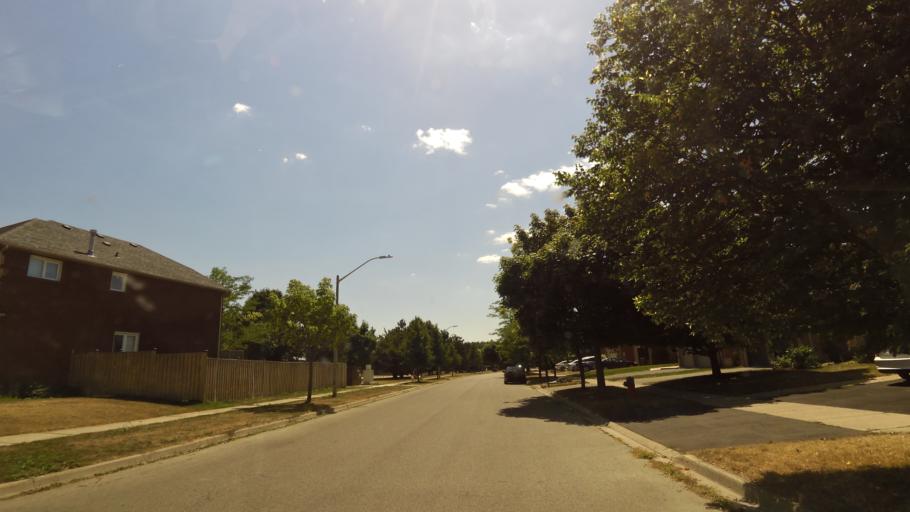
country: CA
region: Ontario
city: Brampton
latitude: 43.6411
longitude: -79.8711
